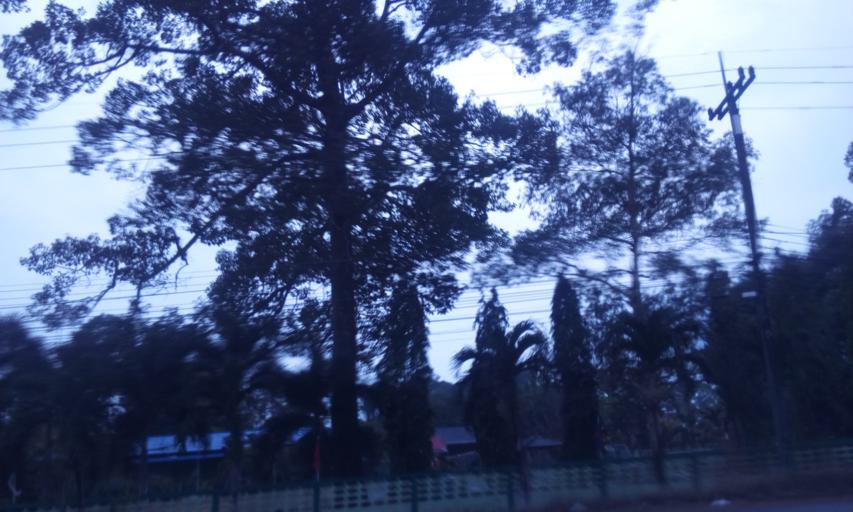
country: TH
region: Trat
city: Khao Saming
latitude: 12.3981
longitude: 102.3495
